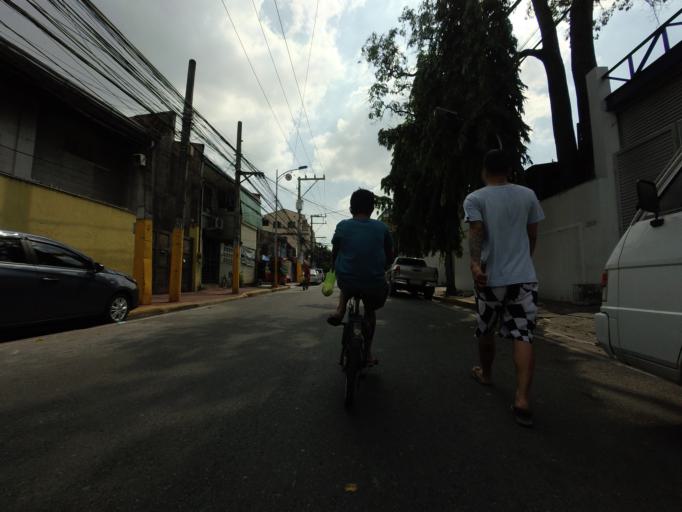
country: PH
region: Metro Manila
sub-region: City of Manila
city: Port Area
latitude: 14.5696
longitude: 120.9954
